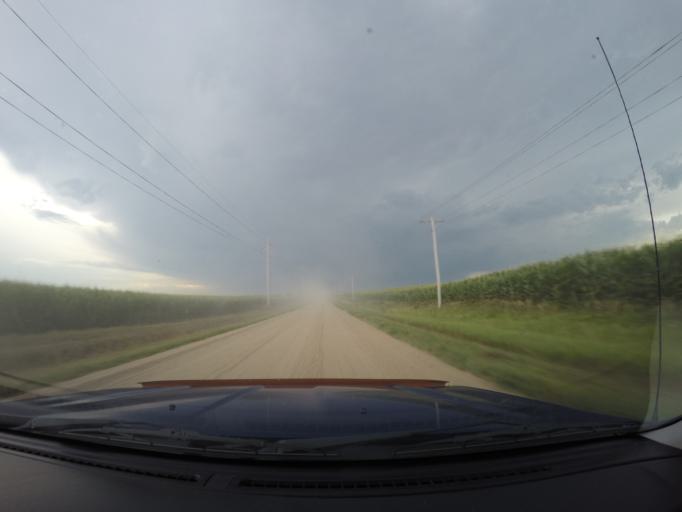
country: US
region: Nebraska
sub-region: Buffalo County
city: Kearney
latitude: 40.8438
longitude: -99.1750
